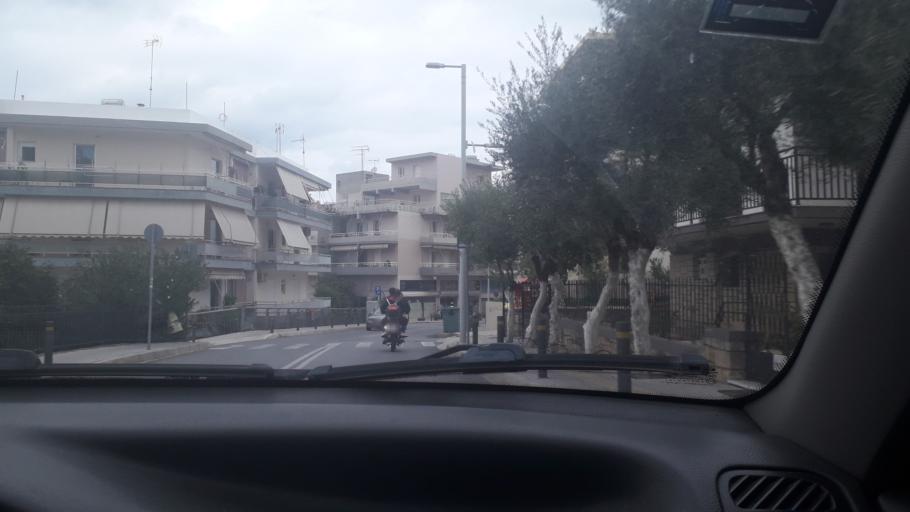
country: GR
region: Crete
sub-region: Nomos Rethymnis
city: Rethymno
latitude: 35.3627
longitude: 24.4726
